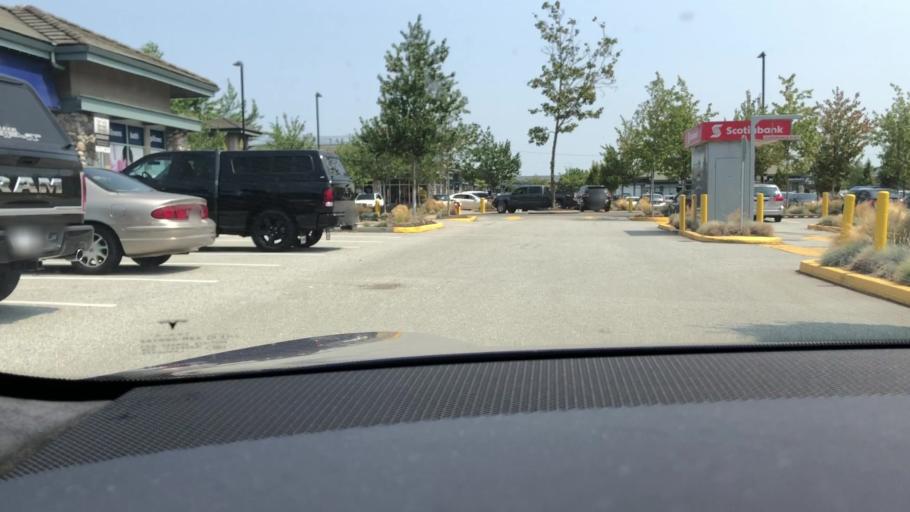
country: CA
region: British Columbia
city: Ladner
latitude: 49.1328
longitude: -123.0954
